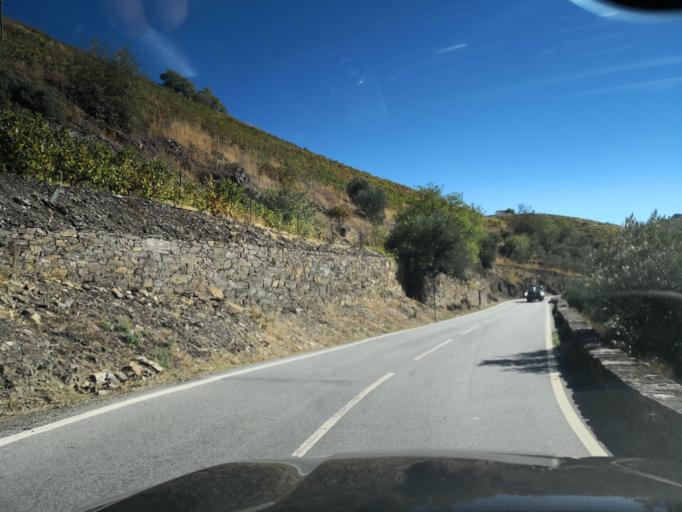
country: PT
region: Viseu
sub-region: Tabuaco
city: Tabuaco
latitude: 41.1723
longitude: -7.5477
